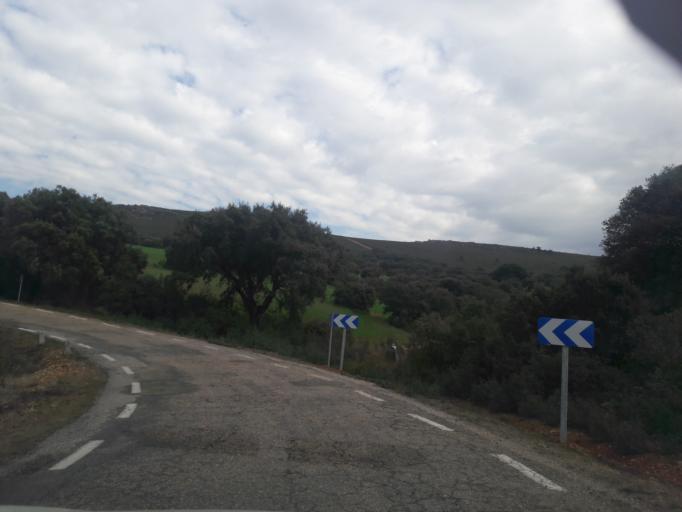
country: ES
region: Castille and Leon
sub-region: Provincia de Salamanca
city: Serradilla del Arroyo
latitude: 40.5384
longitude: -6.3835
